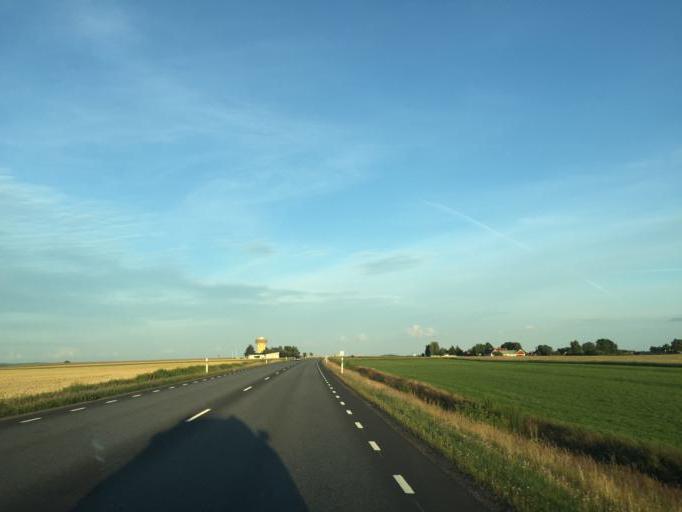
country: SE
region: Skane
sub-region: Angelholms Kommun
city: AEngelholm
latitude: 56.2645
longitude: 12.8778
